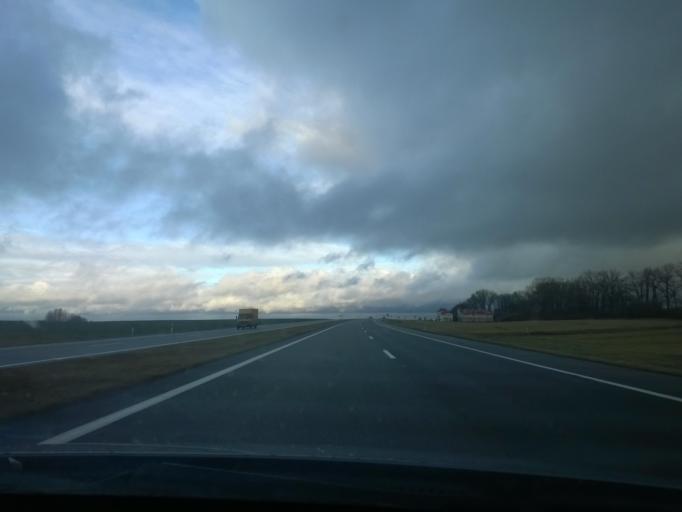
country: BY
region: Brest
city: Baranovichi
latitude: 53.2084
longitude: 26.1124
